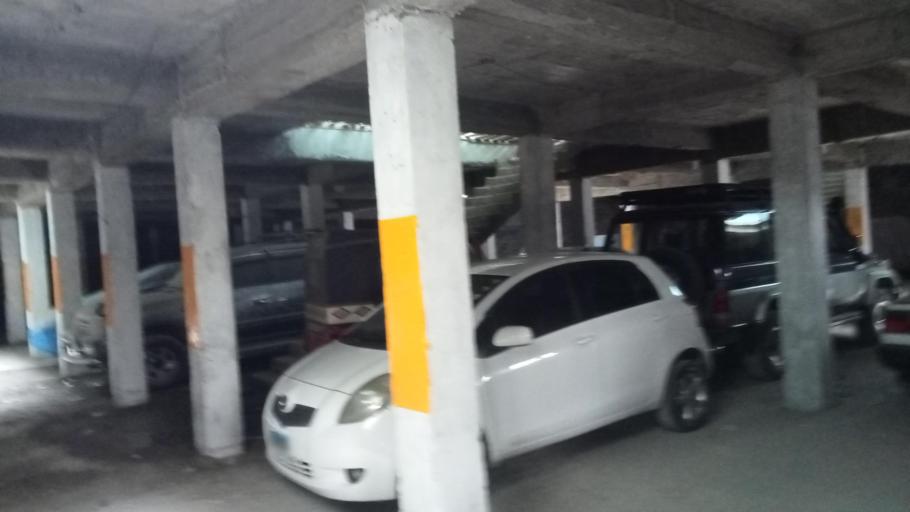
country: PK
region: Khyber Pakhtunkhwa
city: Mingora
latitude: 34.7700
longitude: 72.3398
